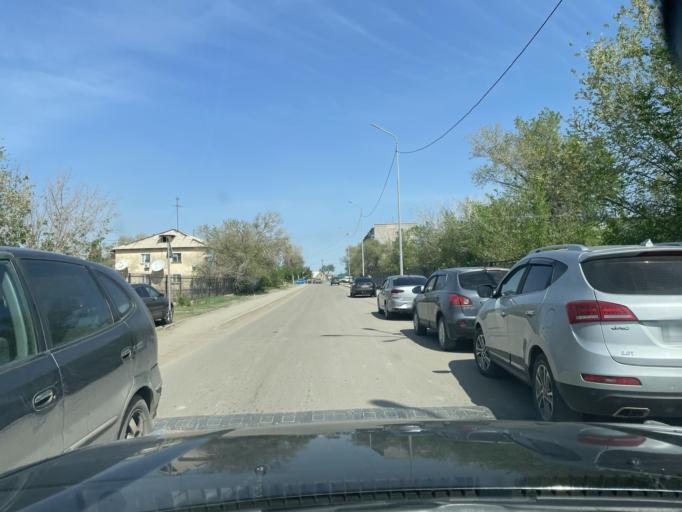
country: KZ
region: Qaraghandy
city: Zhezqazghan
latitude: 47.7873
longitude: 67.6991
